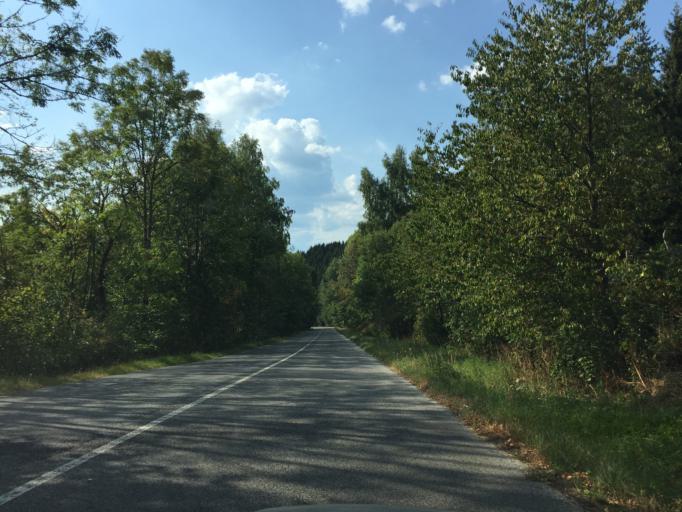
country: CZ
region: Liberecky
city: Mala Skala
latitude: 50.6574
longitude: 15.1645
